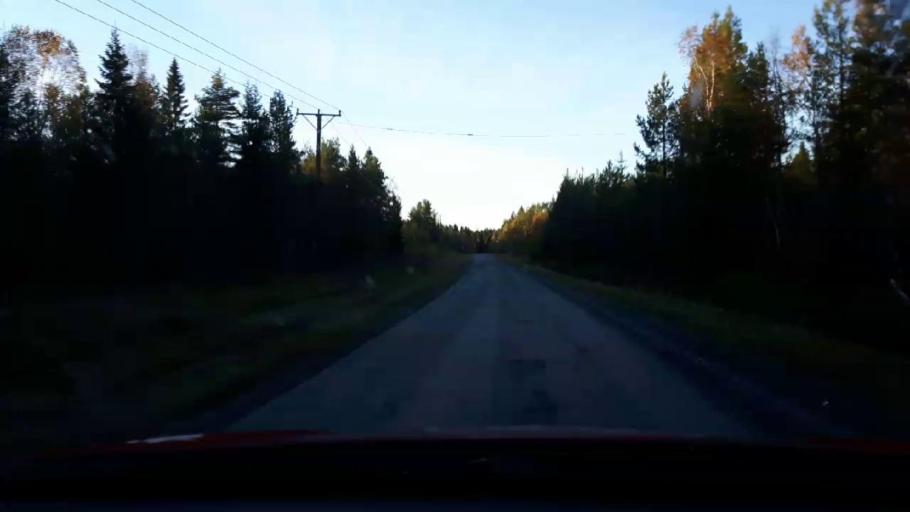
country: SE
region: Jaemtland
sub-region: Krokoms Kommun
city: Krokom
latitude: 63.4492
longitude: 14.4176
